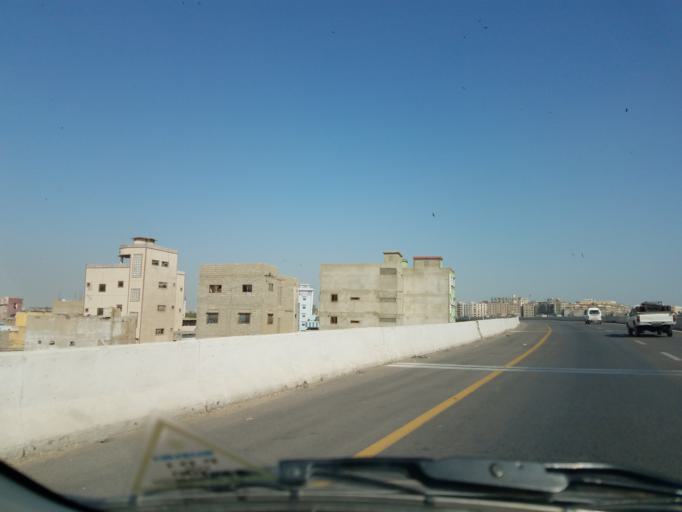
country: PK
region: Sindh
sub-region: Karachi District
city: Karachi
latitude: 24.8800
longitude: 67.0108
